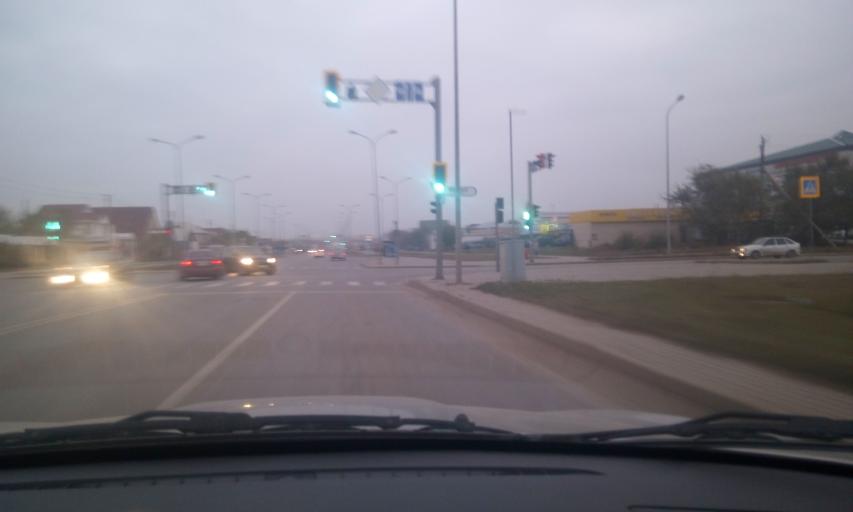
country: KZ
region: Astana Qalasy
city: Astana
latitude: 51.1360
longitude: 71.5122
